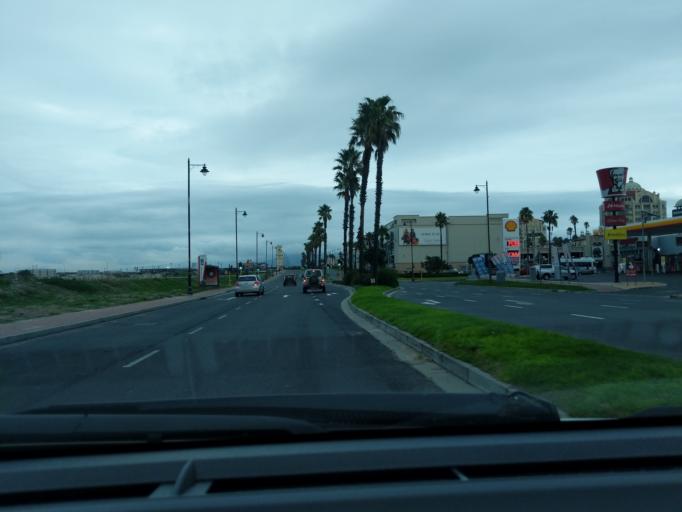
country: ZA
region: Western Cape
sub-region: City of Cape Town
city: Sunset Beach
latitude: -33.8922
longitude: 18.5157
